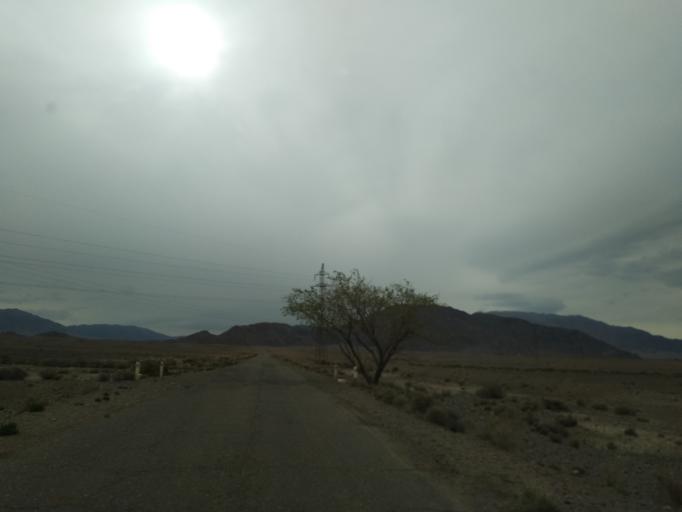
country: KG
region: Ysyk-Koel
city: Balykchy
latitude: 42.3203
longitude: 76.1841
